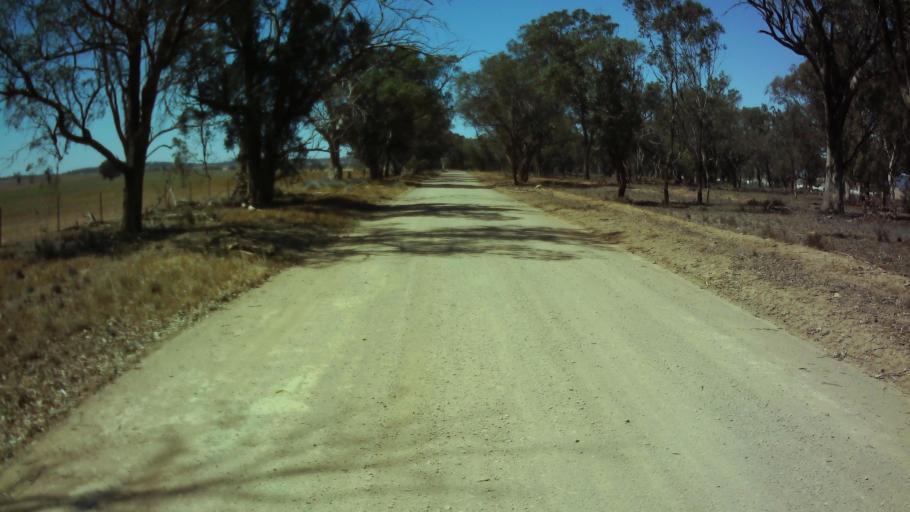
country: AU
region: New South Wales
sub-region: Weddin
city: Grenfell
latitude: -33.8751
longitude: 148.0887
